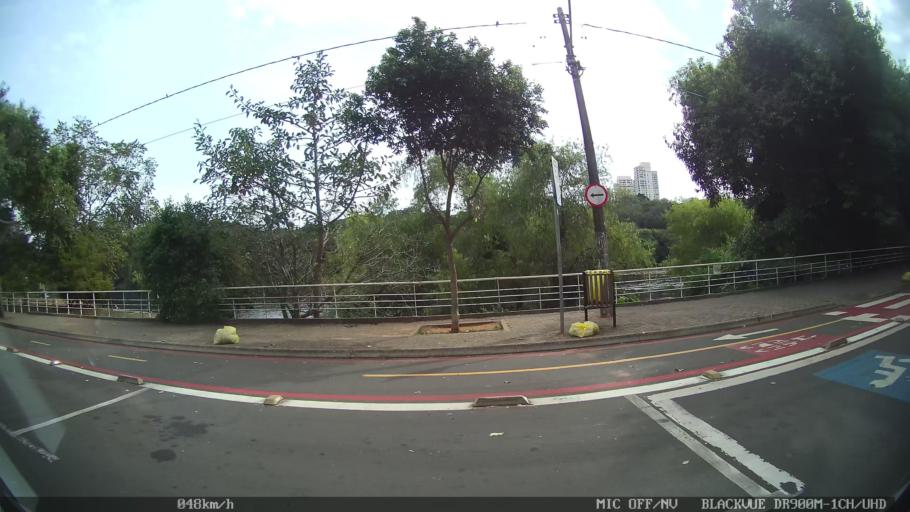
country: BR
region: Sao Paulo
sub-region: Piracicaba
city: Piracicaba
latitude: -22.7211
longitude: -47.6554
